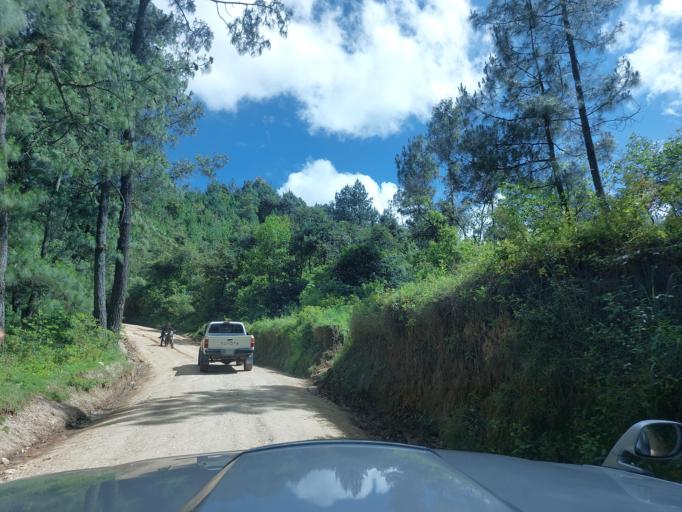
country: GT
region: Chimaltenango
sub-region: Municipio de San Juan Comalapa
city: Comalapa
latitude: 14.7555
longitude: -90.8887
